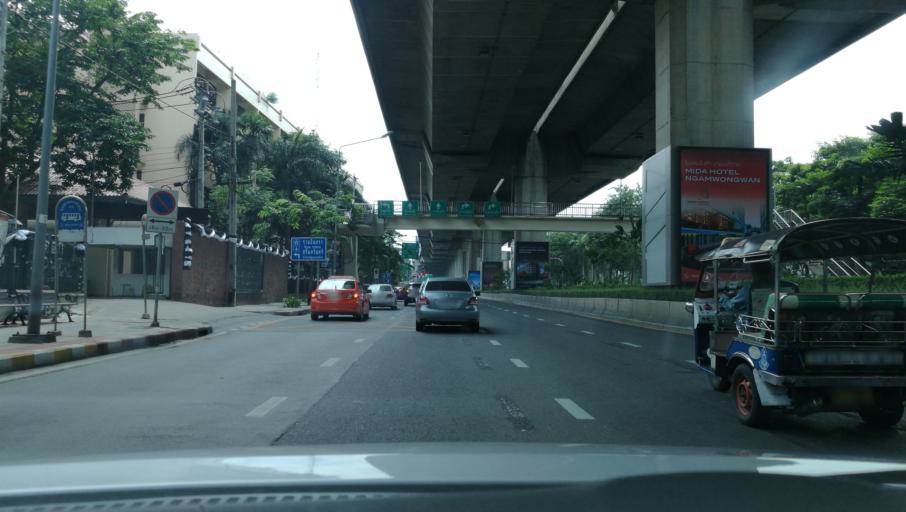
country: TH
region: Bangkok
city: Ratchathewi
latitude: 13.7636
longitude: 100.5266
